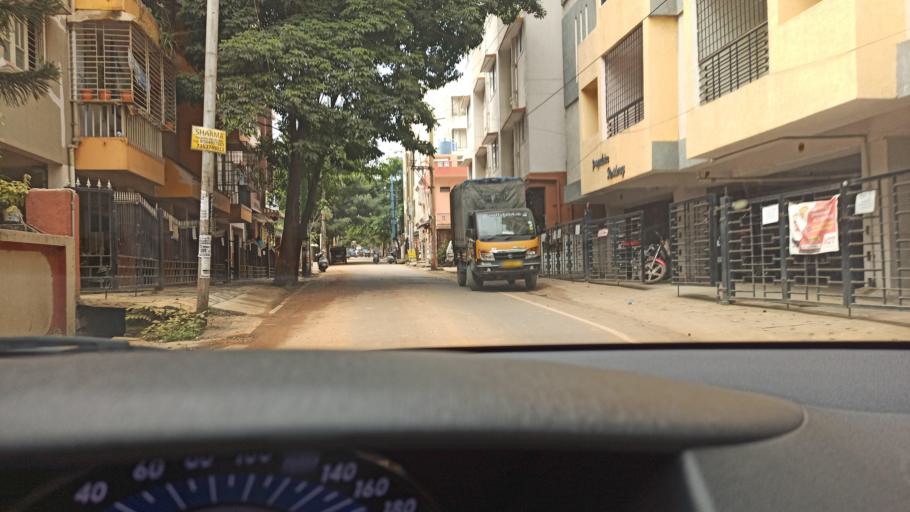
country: IN
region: Karnataka
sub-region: Bangalore Urban
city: Bangalore
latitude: 12.9927
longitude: 77.6829
